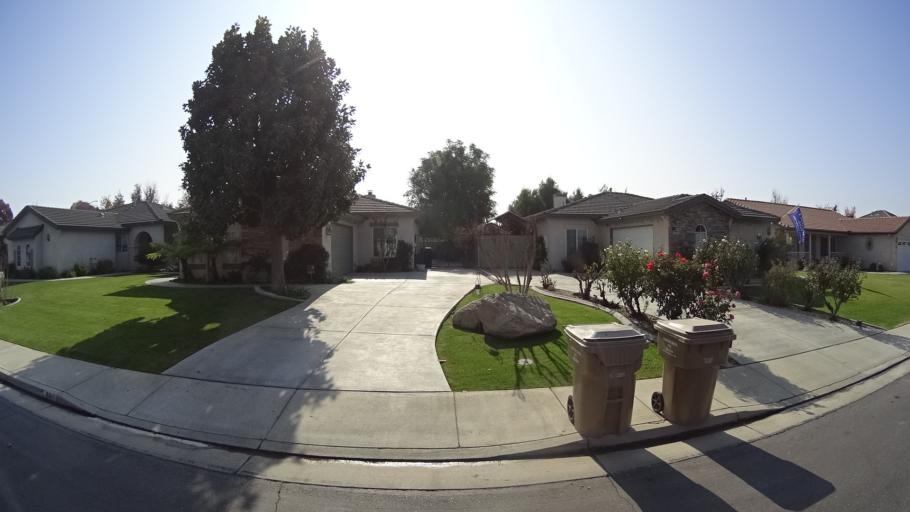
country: US
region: California
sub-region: Kern County
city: Greenacres
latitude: 35.4203
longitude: -119.1117
